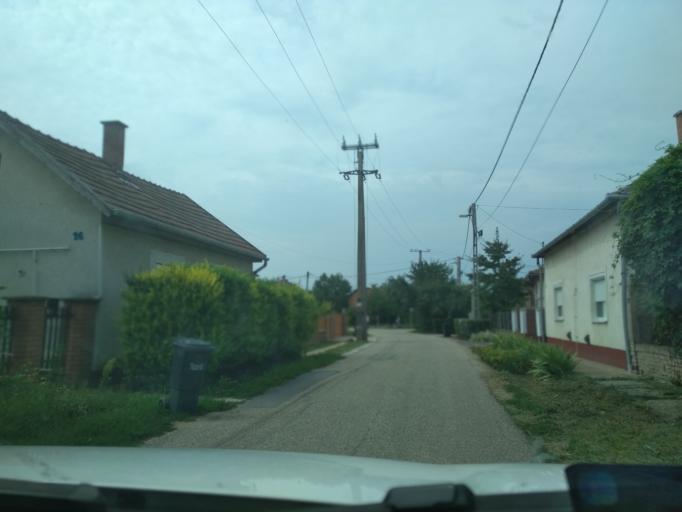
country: HU
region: Jasz-Nagykun-Szolnok
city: Tiszafured
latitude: 47.6171
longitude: 20.7543
